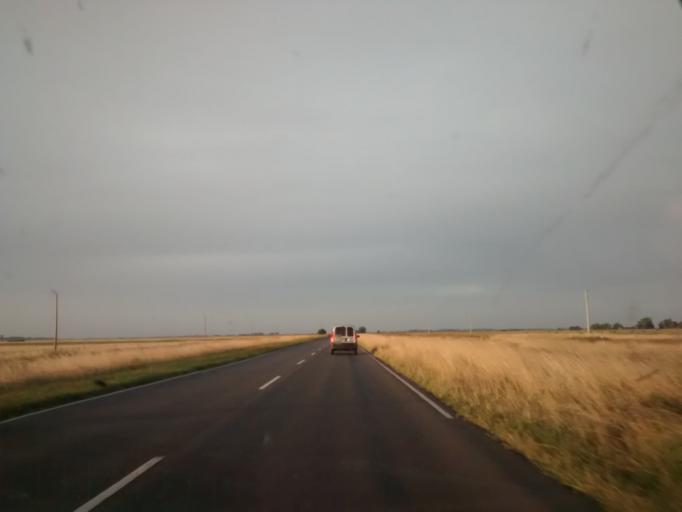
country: AR
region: Buenos Aires
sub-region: Partido de General Belgrano
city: General Belgrano
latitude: -35.9509
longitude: -58.6205
